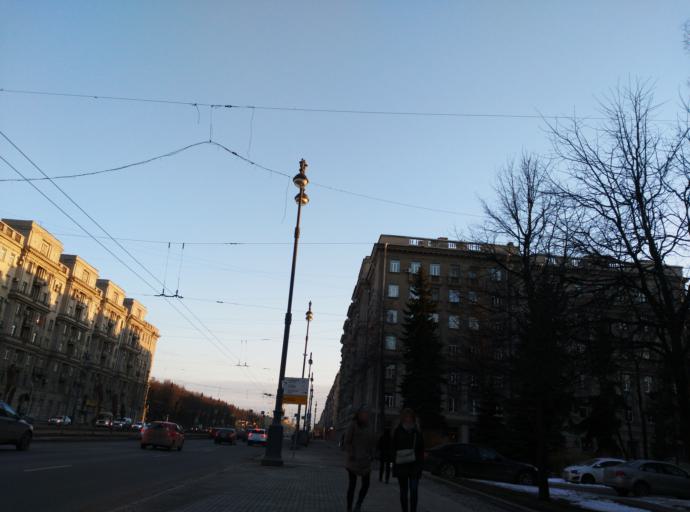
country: RU
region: St.-Petersburg
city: Kupchino
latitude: 59.8734
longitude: 30.3198
